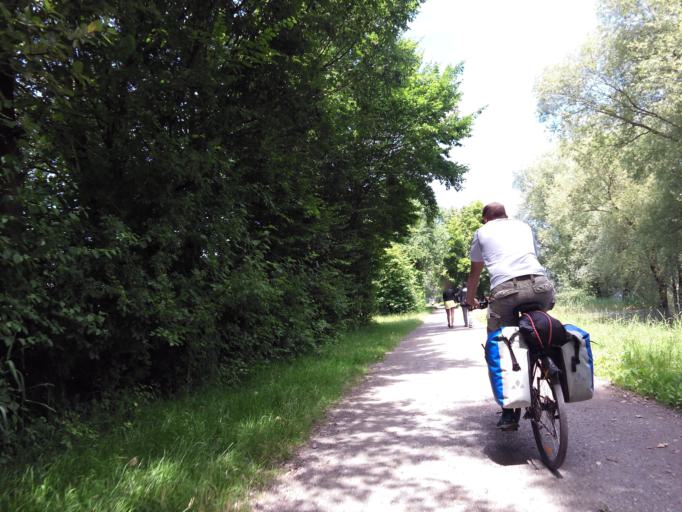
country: AT
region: Vorarlberg
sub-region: Politischer Bezirk Bregenz
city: Hard
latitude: 47.4942
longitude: 9.6785
